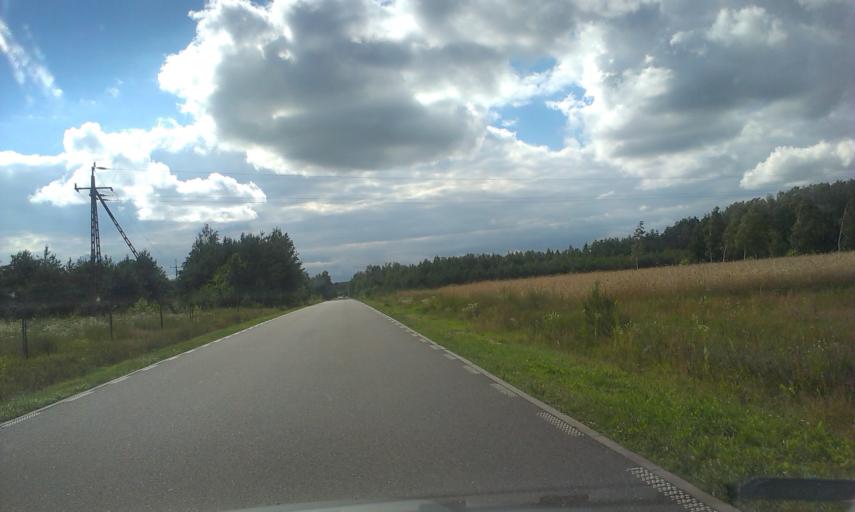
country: PL
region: Lodz Voivodeship
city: Zabia Wola
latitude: 51.9678
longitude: 20.6354
